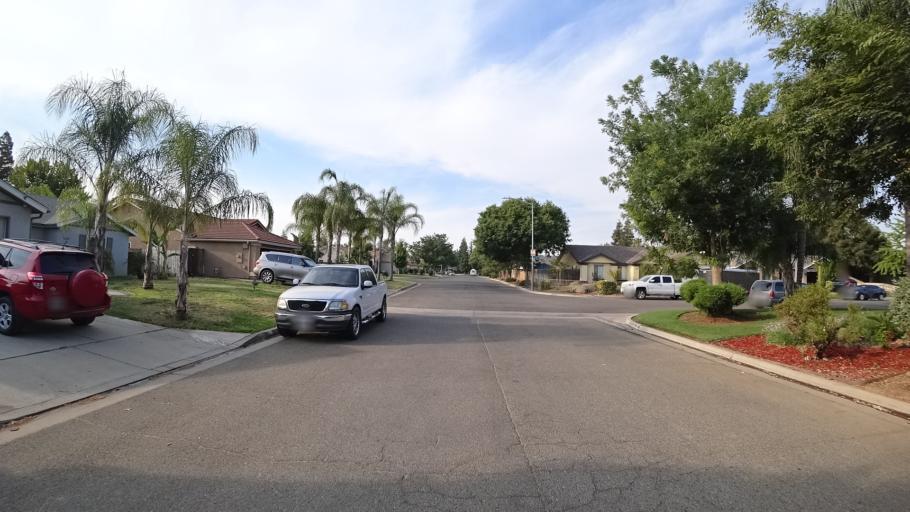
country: US
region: California
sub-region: Fresno County
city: West Park
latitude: 36.7702
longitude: -119.8561
